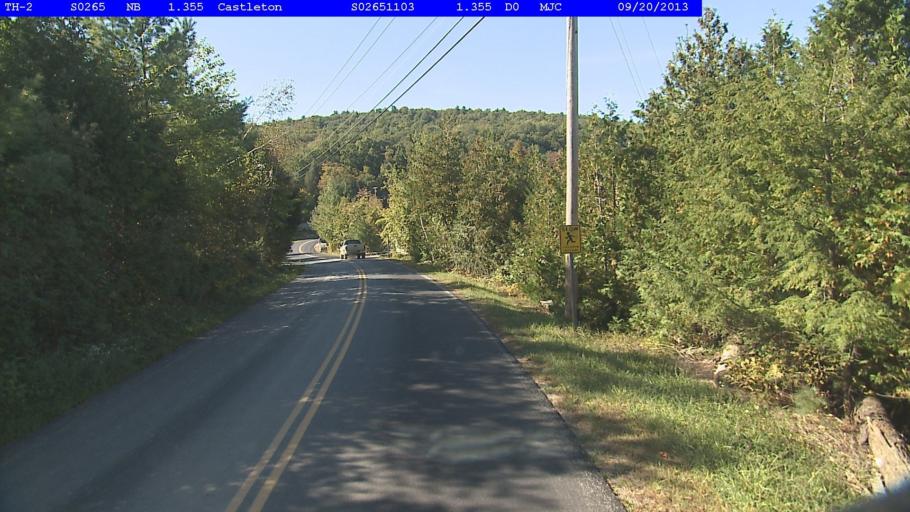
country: US
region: Vermont
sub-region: Rutland County
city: Fair Haven
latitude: 43.6232
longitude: -73.2307
